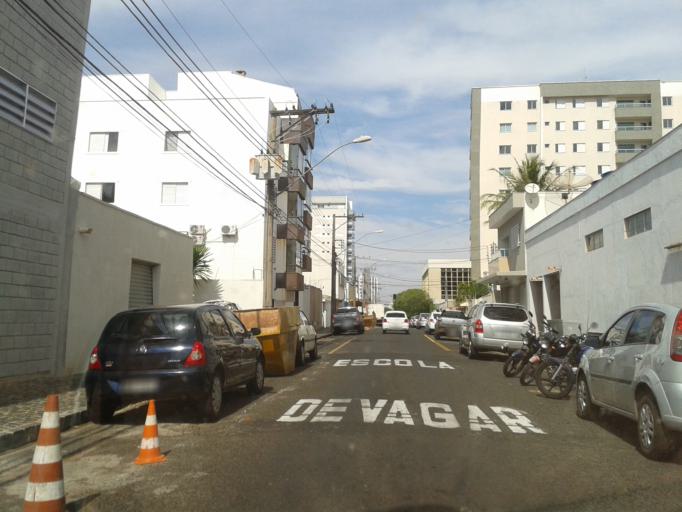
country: BR
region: Minas Gerais
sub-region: Uberlandia
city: Uberlandia
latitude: -18.9096
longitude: -48.2711
